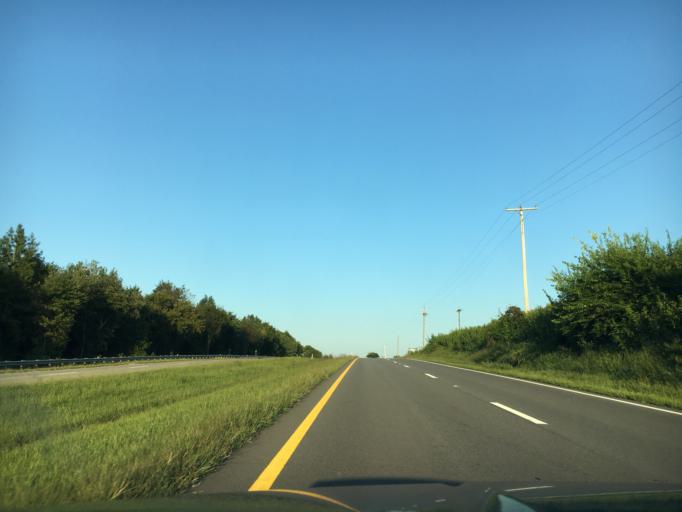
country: US
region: Virginia
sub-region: City of Danville
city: Danville
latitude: 36.5807
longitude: -79.1861
